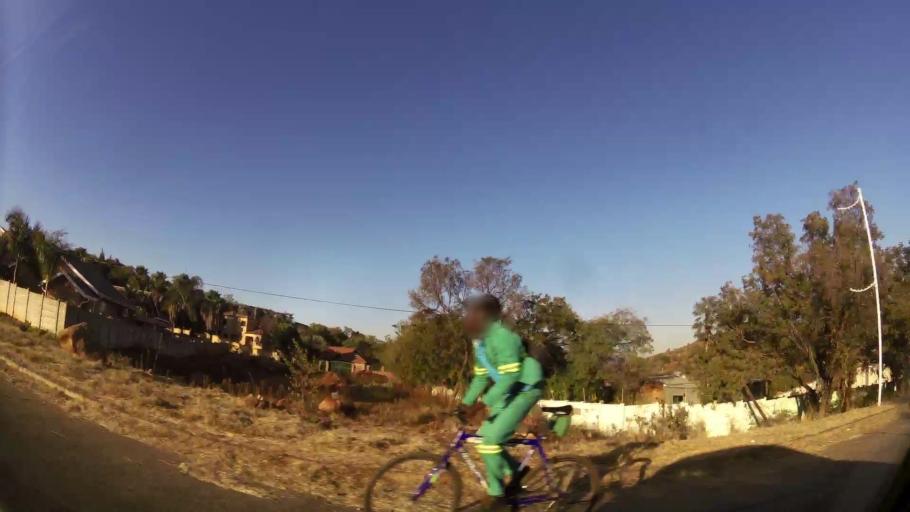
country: ZA
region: North-West
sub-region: Bojanala Platinum District Municipality
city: Rustenburg
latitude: -25.7079
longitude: 27.2398
